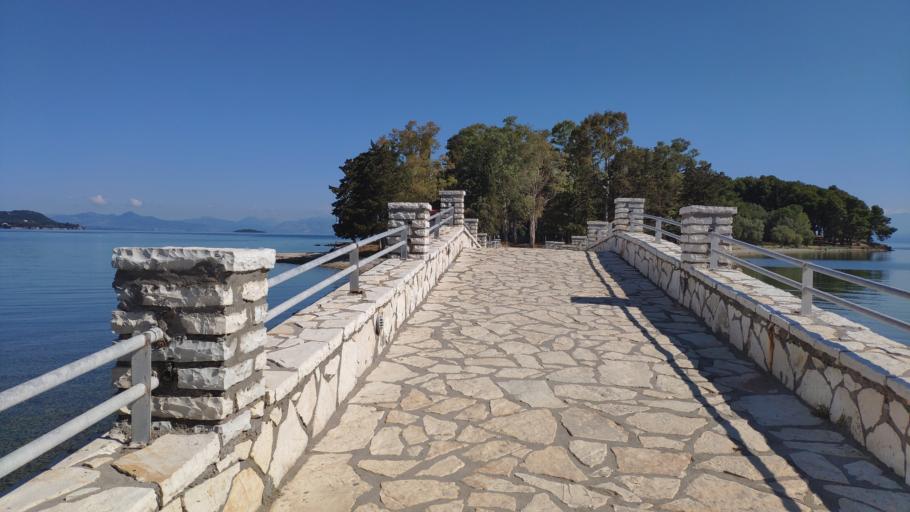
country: GR
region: West Greece
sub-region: Nomos Aitolias kai Akarnanias
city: Vonitsa
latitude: 38.9238
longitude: 20.9001
